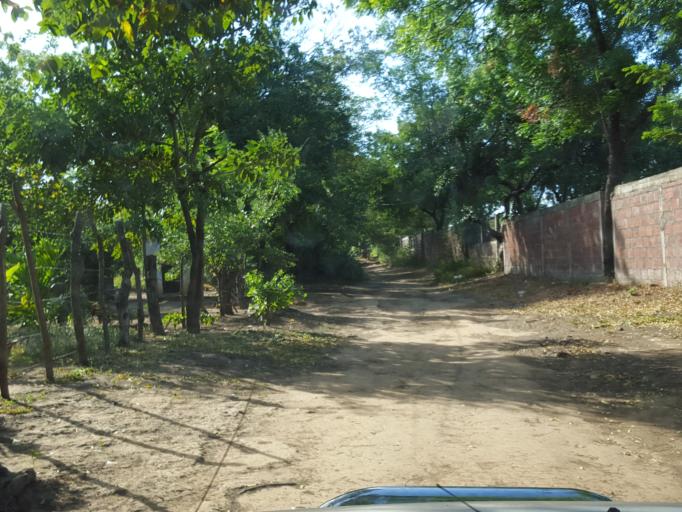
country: NI
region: Leon
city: Leon
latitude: 12.4214
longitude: -86.9092
